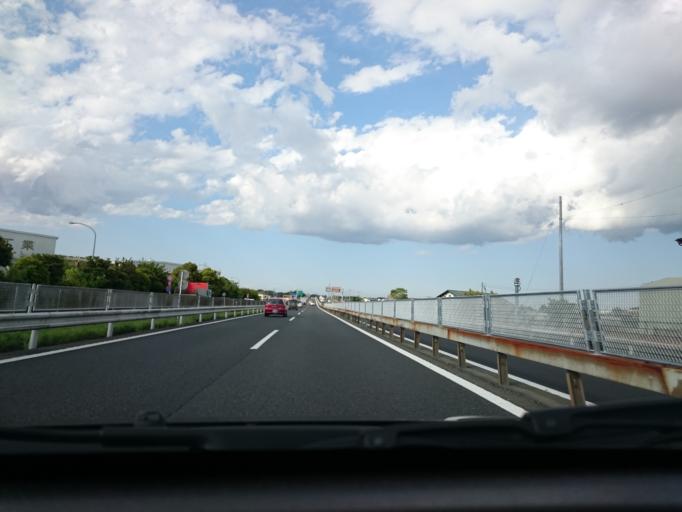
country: JP
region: Kanagawa
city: Isehara
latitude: 35.3661
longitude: 139.3087
